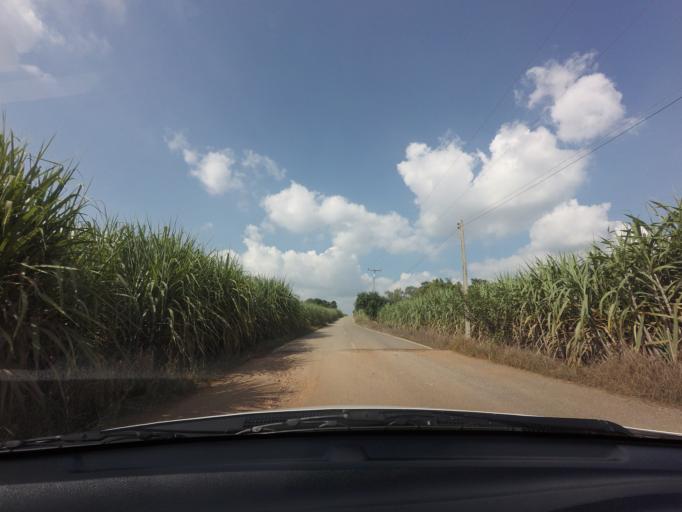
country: TH
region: Nakhon Ratchasima
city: Wang Nam Khiao
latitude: 14.5095
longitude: 101.6302
